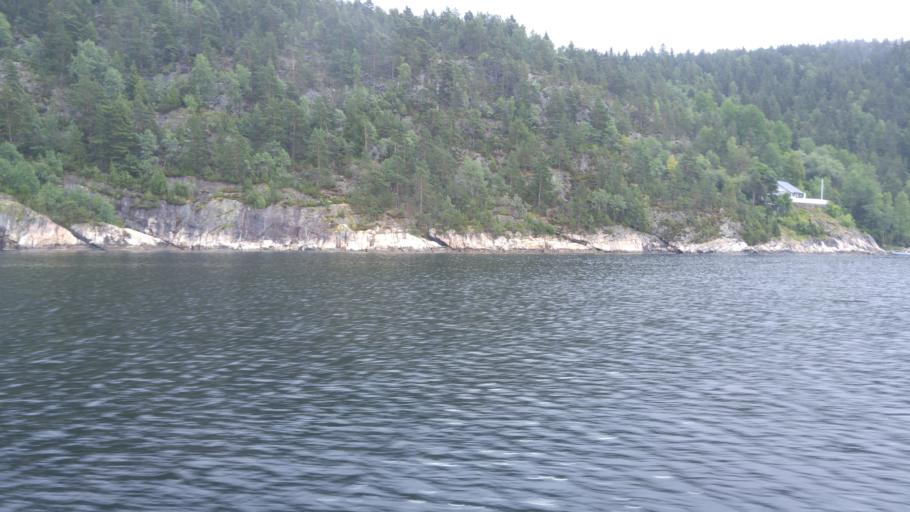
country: NO
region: Akershus
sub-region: Nesodden
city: Nesoddtangen
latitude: 59.8141
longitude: 10.6143
